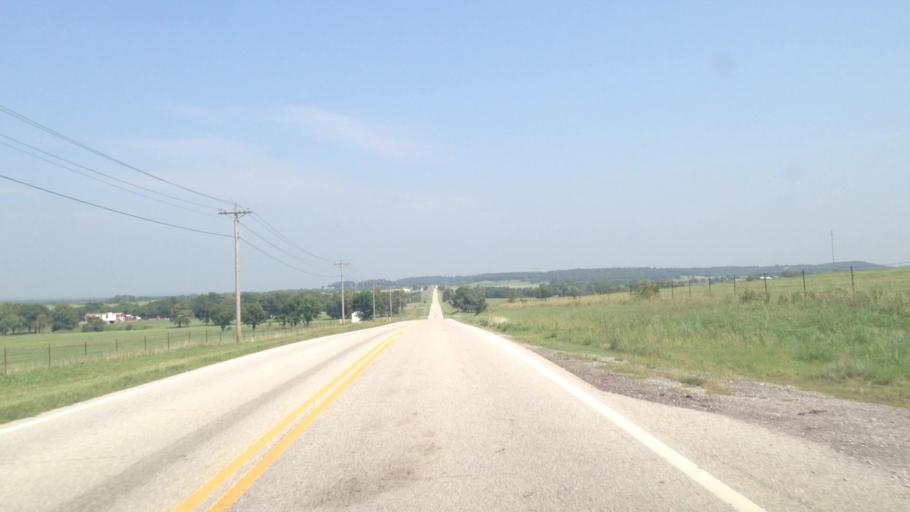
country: US
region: Oklahoma
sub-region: Craig County
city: Vinita
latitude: 36.7405
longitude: -95.1434
